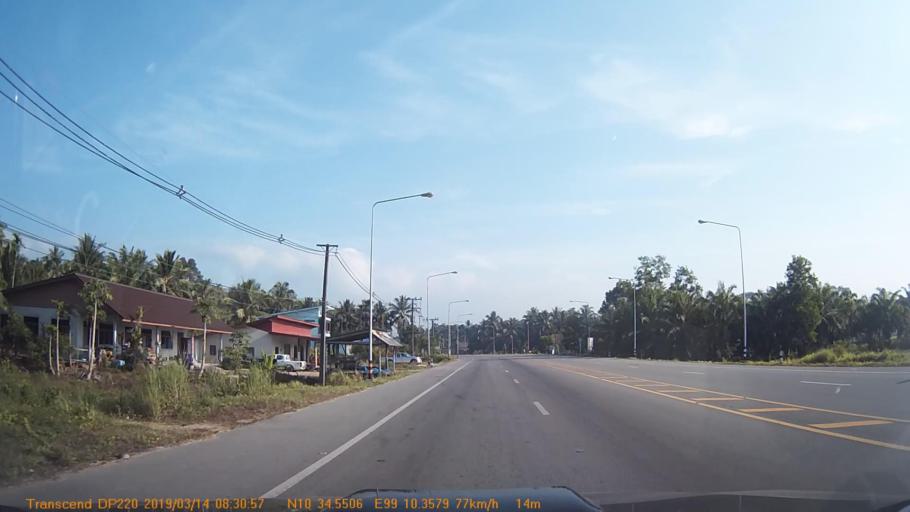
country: TH
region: Chumphon
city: Chumphon
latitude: 10.5762
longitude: 99.1726
